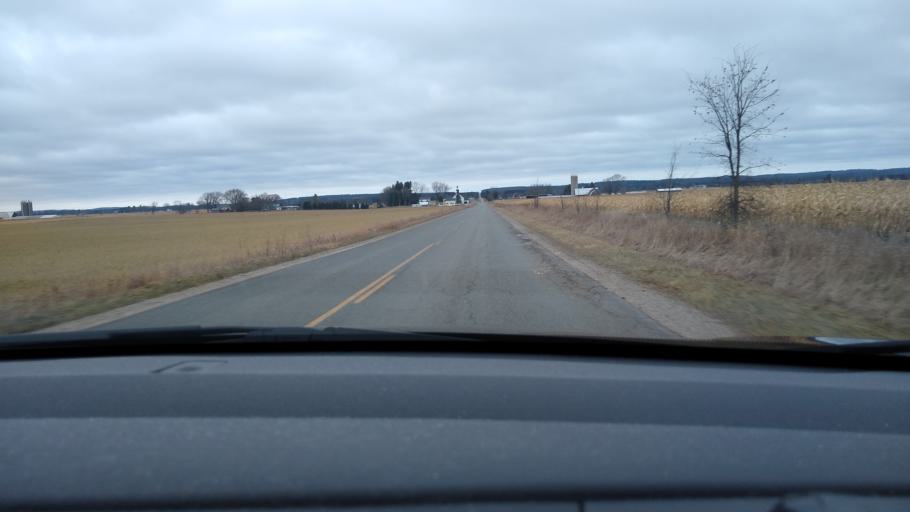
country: US
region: Michigan
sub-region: Missaukee County
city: Lake City
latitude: 44.2368
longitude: -85.0534
